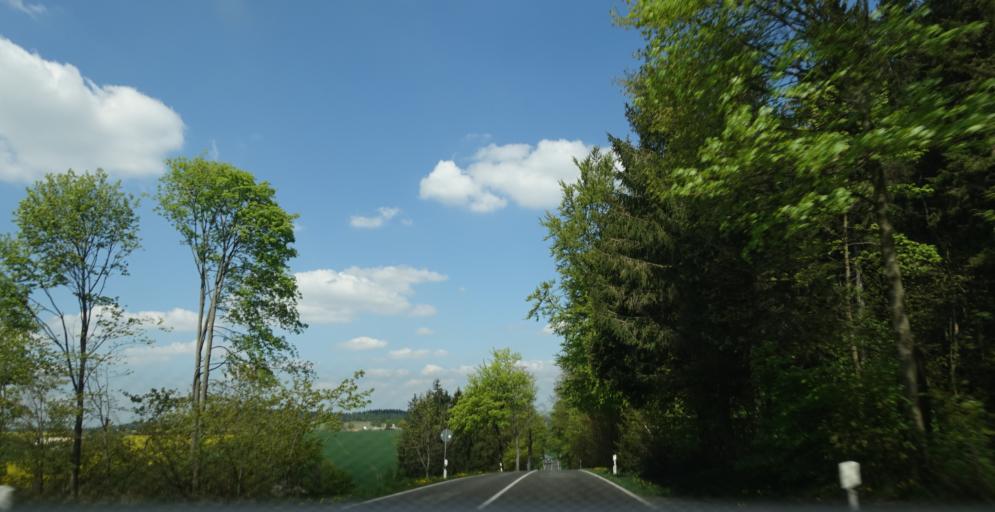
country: DE
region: Saxony
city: Bornichen
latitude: 50.7373
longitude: 13.1355
